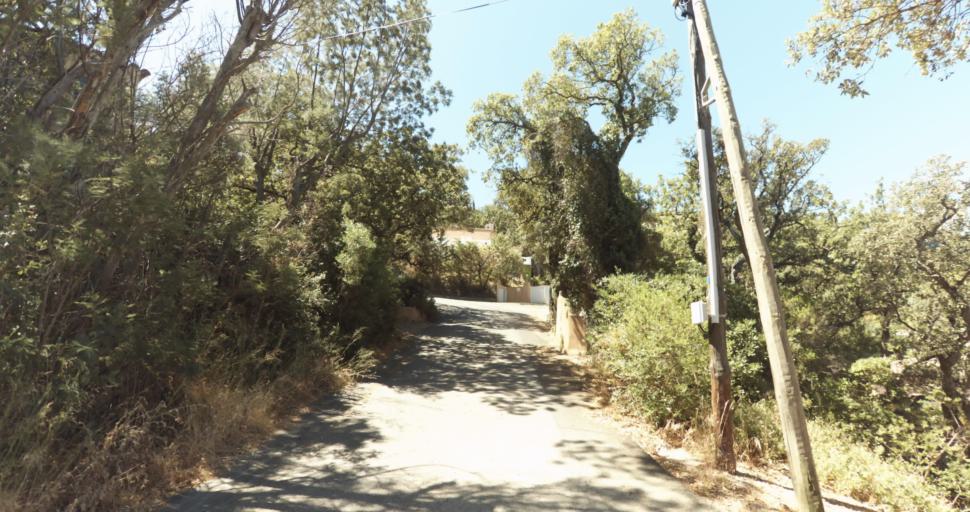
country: FR
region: Provence-Alpes-Cote d'Azur
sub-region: Departement du Var
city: Saint-Tropez
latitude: 43.2609
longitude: 6.6046
